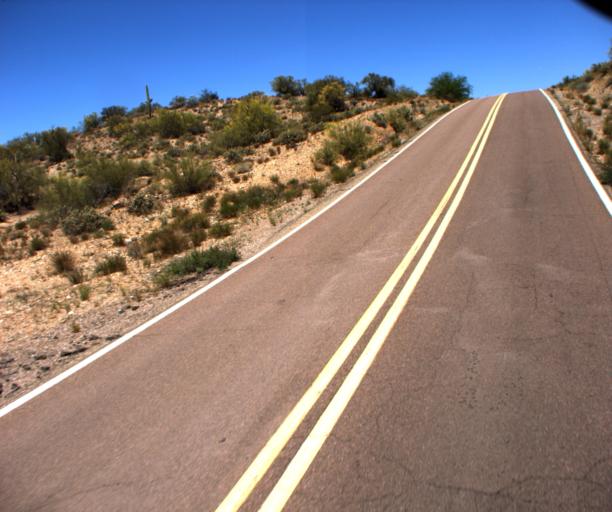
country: US
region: Arizona
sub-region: Yavapai County
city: Bagdad
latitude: 34.4387
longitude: -113.2405
